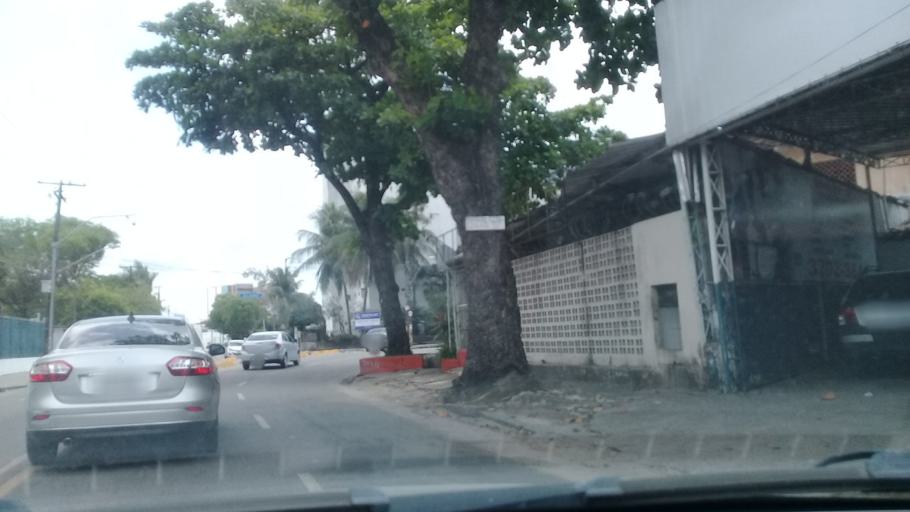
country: BR
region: Pernambuco
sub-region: Recife
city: Recife
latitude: -8.1073
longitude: -34.9153
